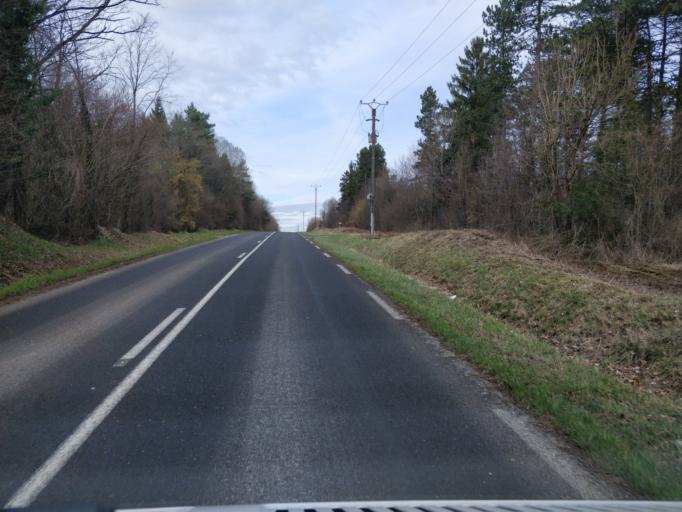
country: FR
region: Lorraine
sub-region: Departement de Meurthe-et-Moselle
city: Montauville
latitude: 48.9162
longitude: 5.9198
